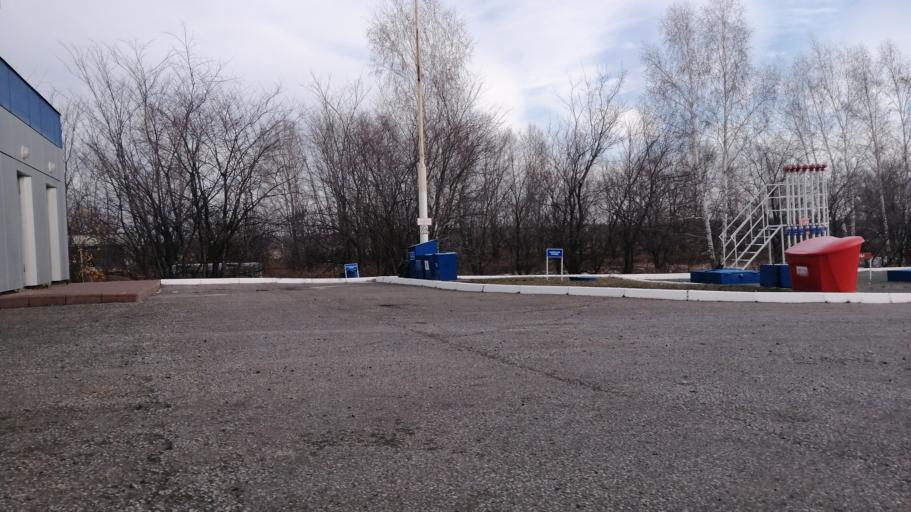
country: RU
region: Novosibirsk
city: Krasnozerskoye
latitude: 53.9839
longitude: 78.7320
